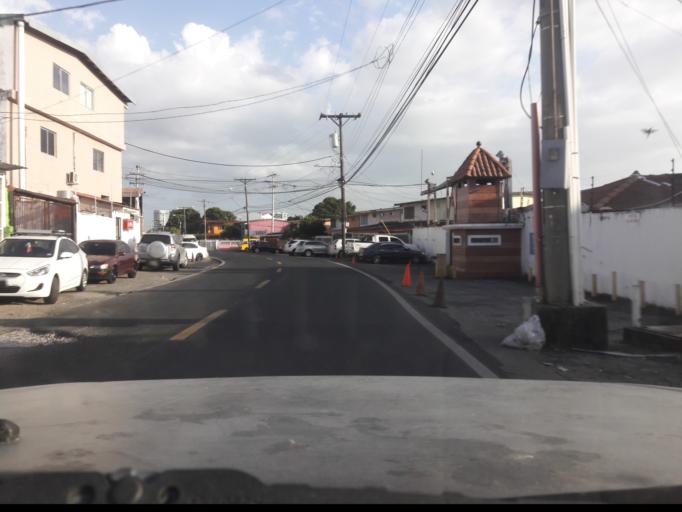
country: PA
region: Panama
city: San Miguelito
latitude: 9.0246
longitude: -79.4953
